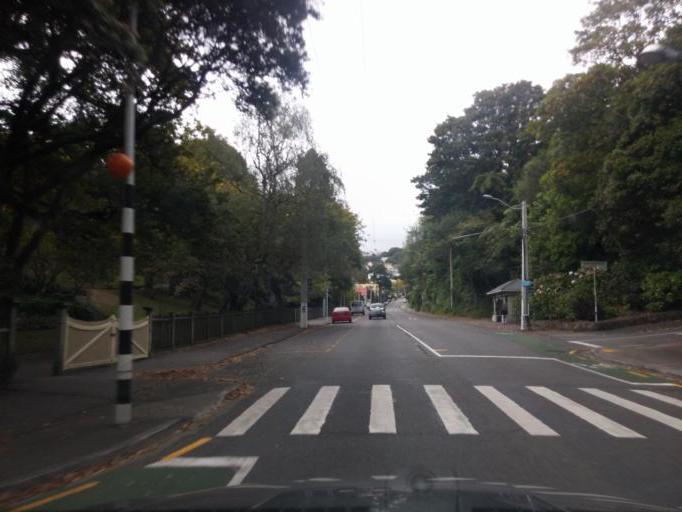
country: NZ
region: Wellington
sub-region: Wellington City
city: Kelburn
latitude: -41.2832
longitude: 174.7626
